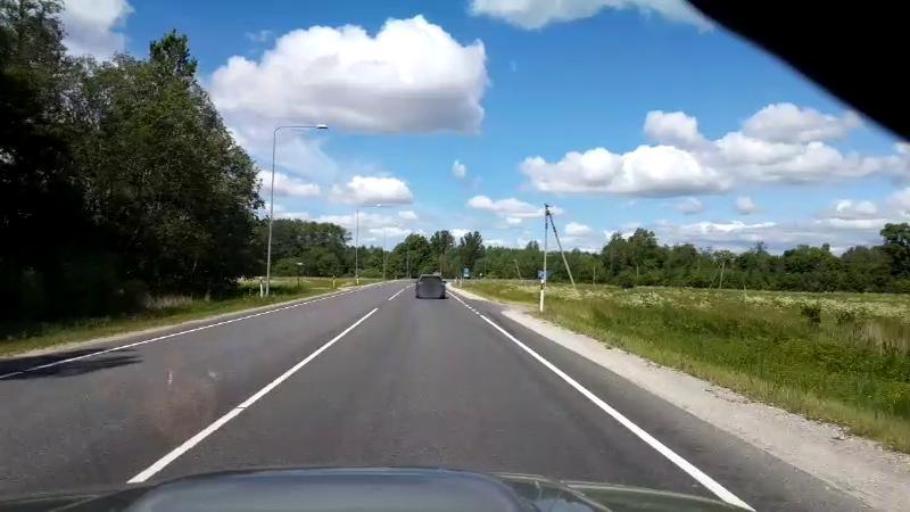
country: EE
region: Paernumaa
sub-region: Sauga vald
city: Sauga
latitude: 58.4451
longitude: 24.4985
